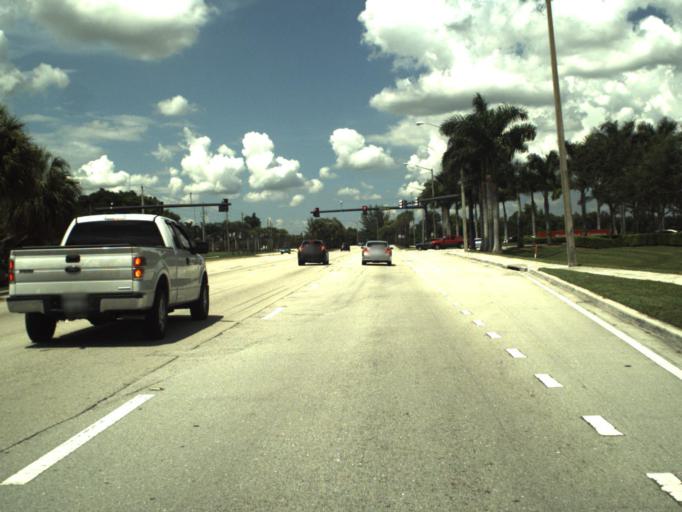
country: US
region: Florida
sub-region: Miami-Dade County
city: Country Club
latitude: 25.9806
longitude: -80.2853
